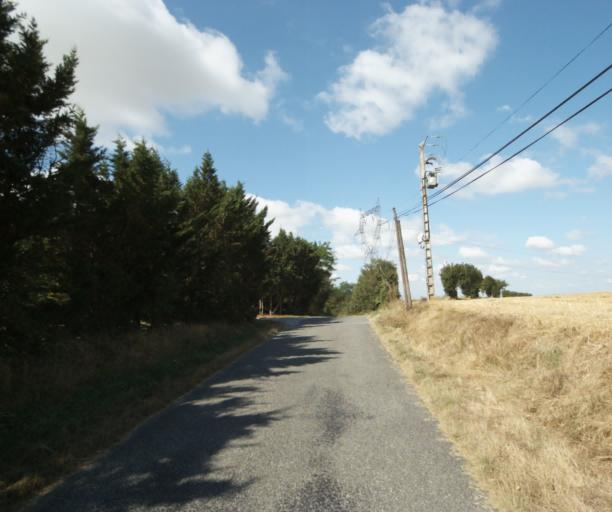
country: FR
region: Midi-Pyrenees
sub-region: Departement de la Haute-Garonne
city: Saint-Felix-Lauragais
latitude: 43.4536
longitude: 1.8340
